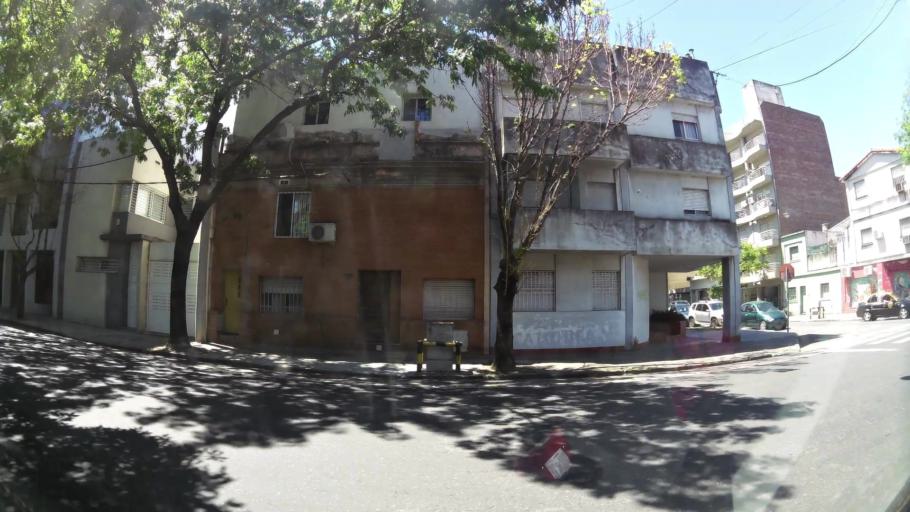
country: AR
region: Santa Fe
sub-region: Departamento de Rosario
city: Rosario
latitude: -32.9455
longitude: -60.6594
